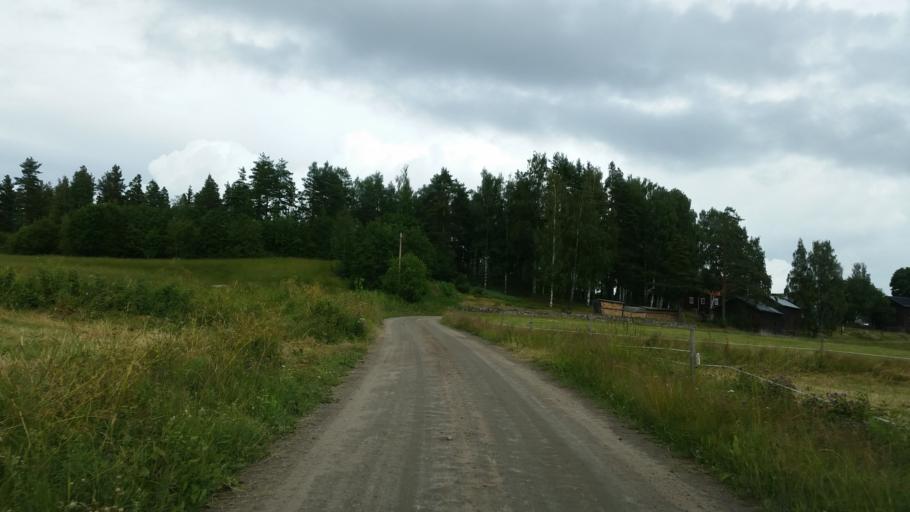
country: SE
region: Gaevleborg
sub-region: Hudiksvalls Kommun
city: Delsbo
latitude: 61.8059
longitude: 16.5333
